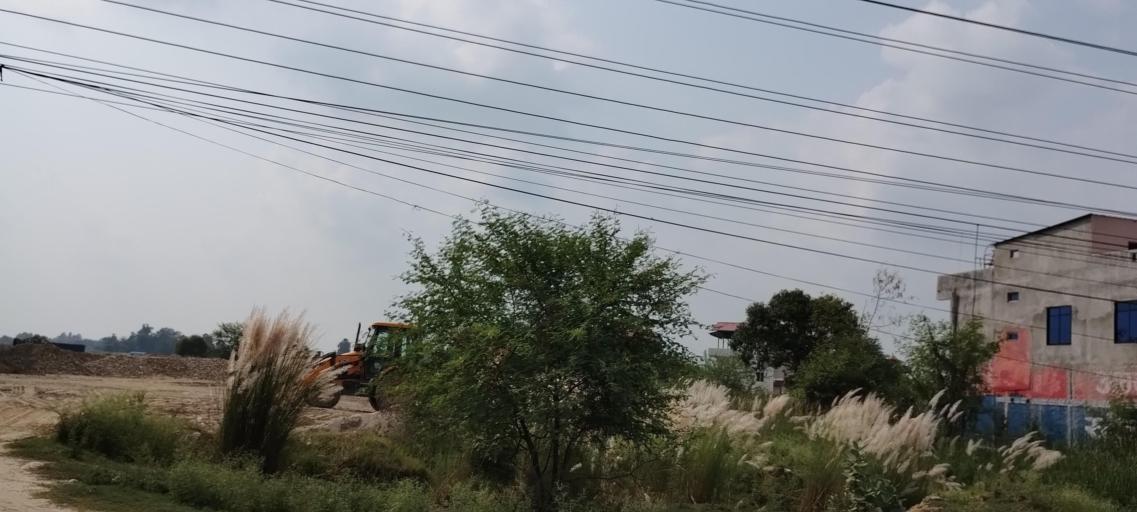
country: NP
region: Mid Western
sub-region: Bheri Zone
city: Nepalgunj
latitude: 28.1593
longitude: 81.6708
